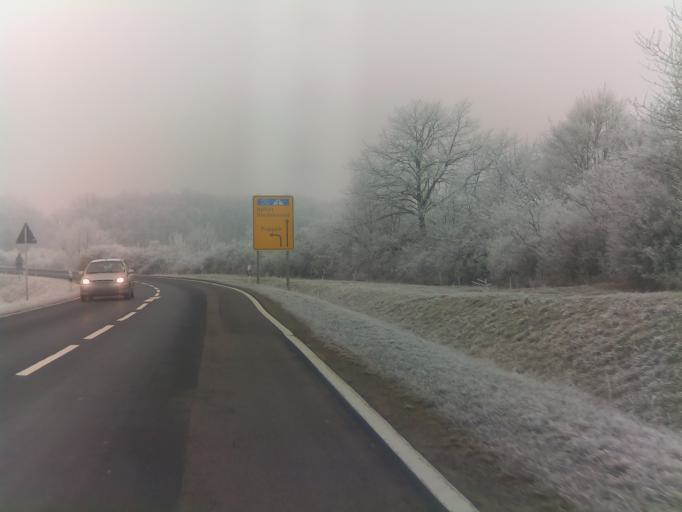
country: DE
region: Bavaria
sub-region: Regierungsbezirk Unterfranken
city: Hassfurt
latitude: 50.0657
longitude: 10.5506
